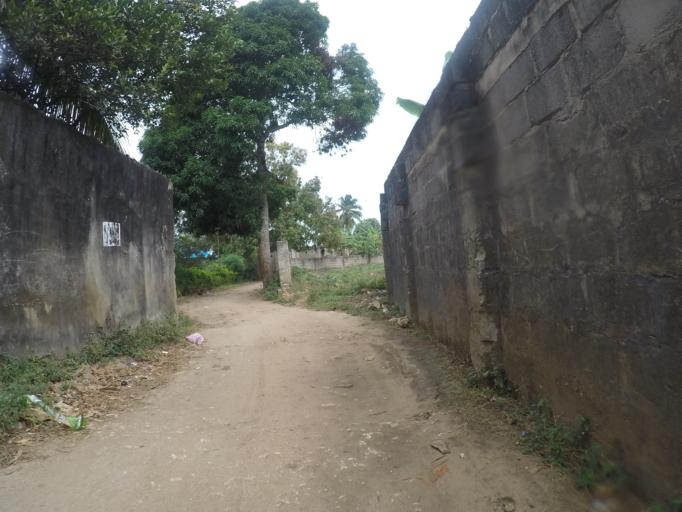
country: TZ
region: Zanzibar Urban/West
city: Zanzibar
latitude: -6.2126
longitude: 39.2168
